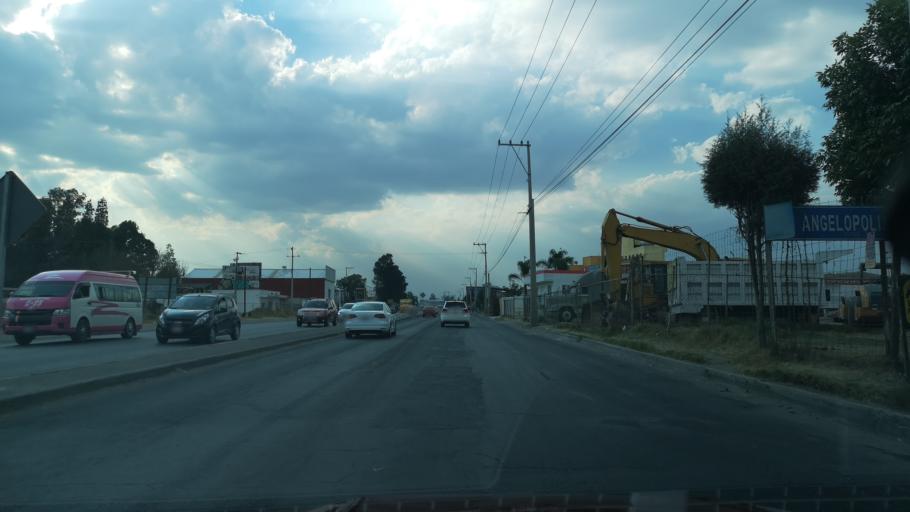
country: MX
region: Puebla
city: Cholula
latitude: 19.0733
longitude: -98.3176
